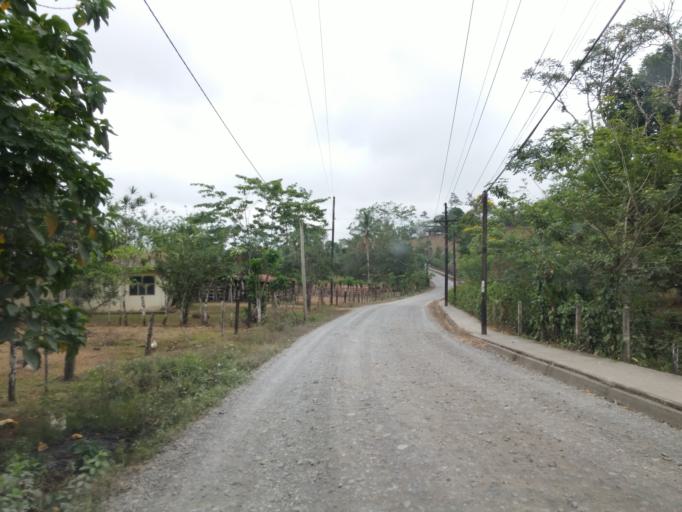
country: CR
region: Alajuela
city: Quesada
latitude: 10.3177
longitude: -84.5199
